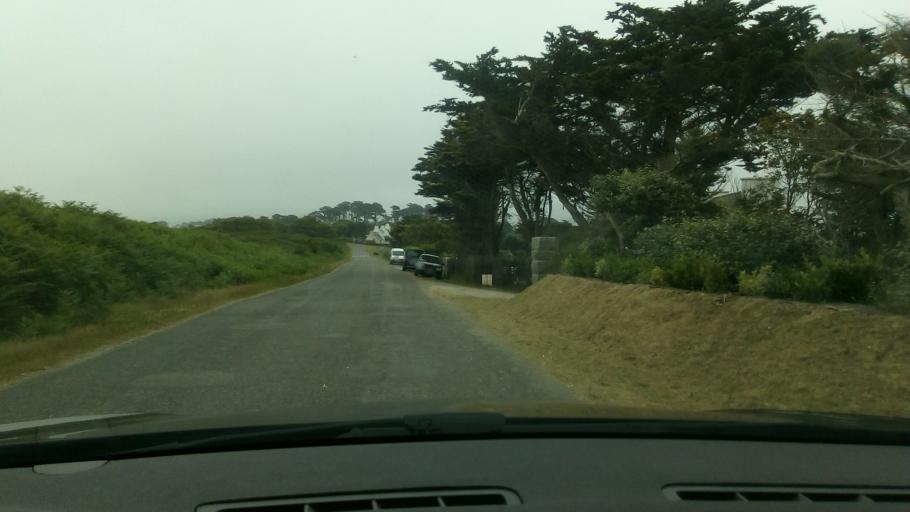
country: FR
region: Brittany
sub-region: Departement du Finistere
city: Le Conquet
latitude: 48.3641
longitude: -4.7719
